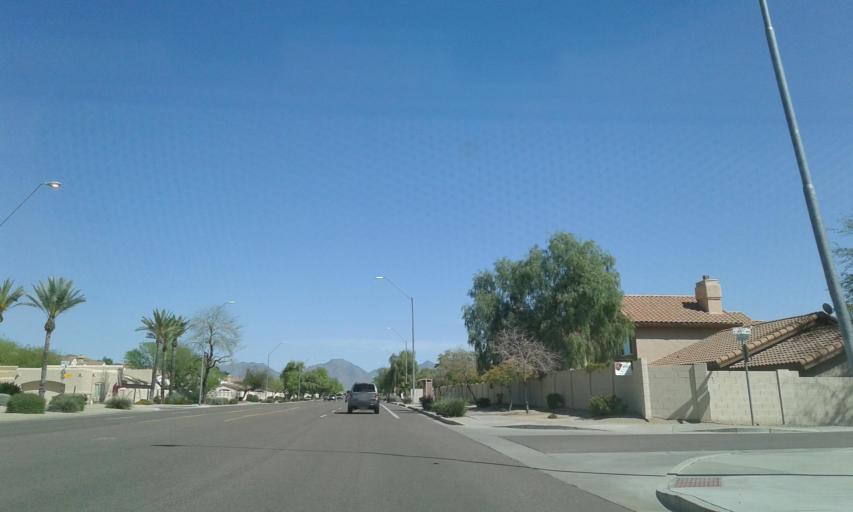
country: US
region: Arizona
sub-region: Maricopa County
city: Paradise Valley
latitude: 33.6551
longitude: -111.9832
